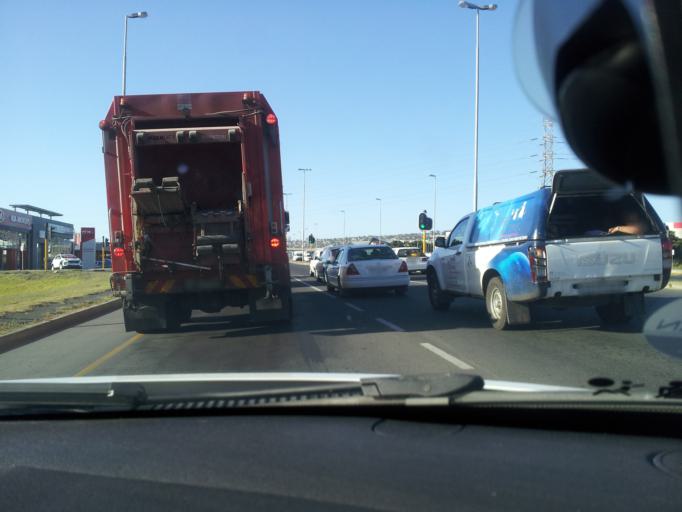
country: ZA
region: Western Cape
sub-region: Cape Winelands District Municipality
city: Stellenbosch
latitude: -34.0854
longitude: 18.8199
